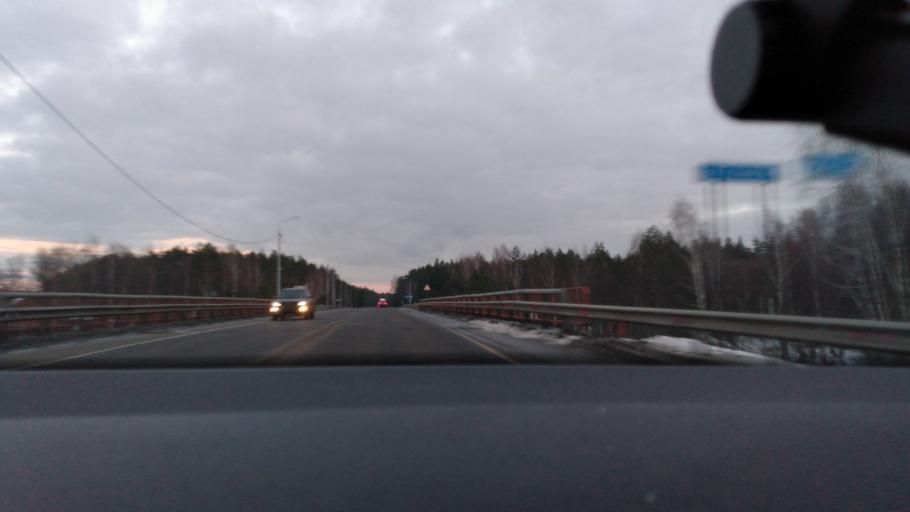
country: RU
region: Moskovskaya
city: Il'inskiy Pogost
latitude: 55.4787
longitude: 38.9411
